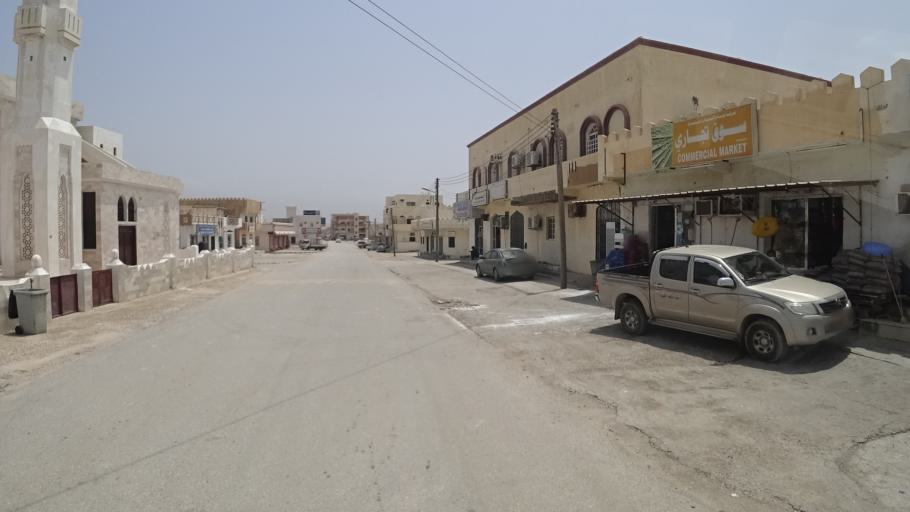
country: OM
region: Zufar
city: Salalah
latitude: 16.9824
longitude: 54.6921
